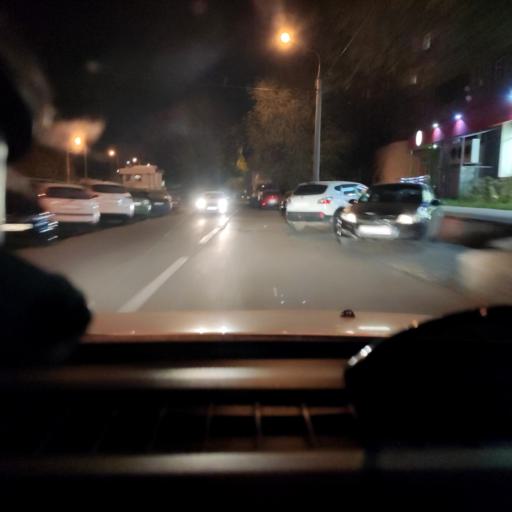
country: RU
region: Samara
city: Samara
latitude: 53.1939
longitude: 50.1996
